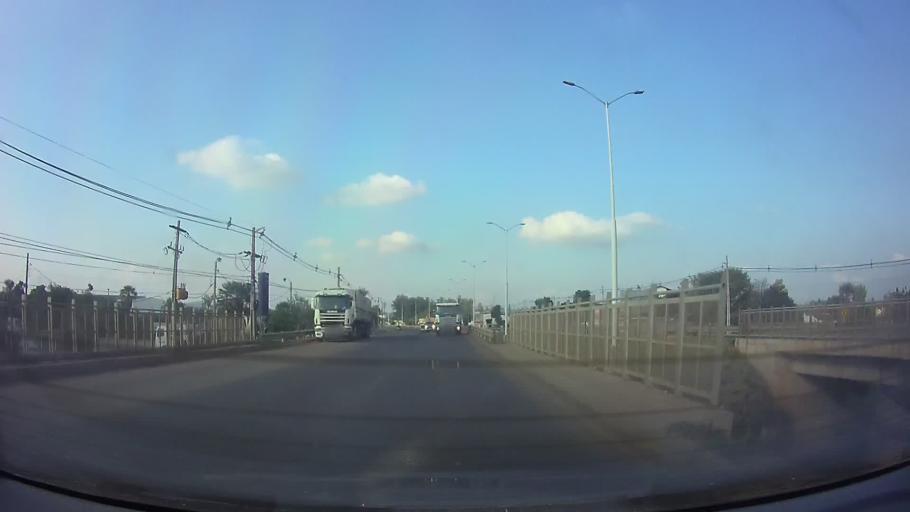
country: PY
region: Central
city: Limpio
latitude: -25.1900
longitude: -57.5006
